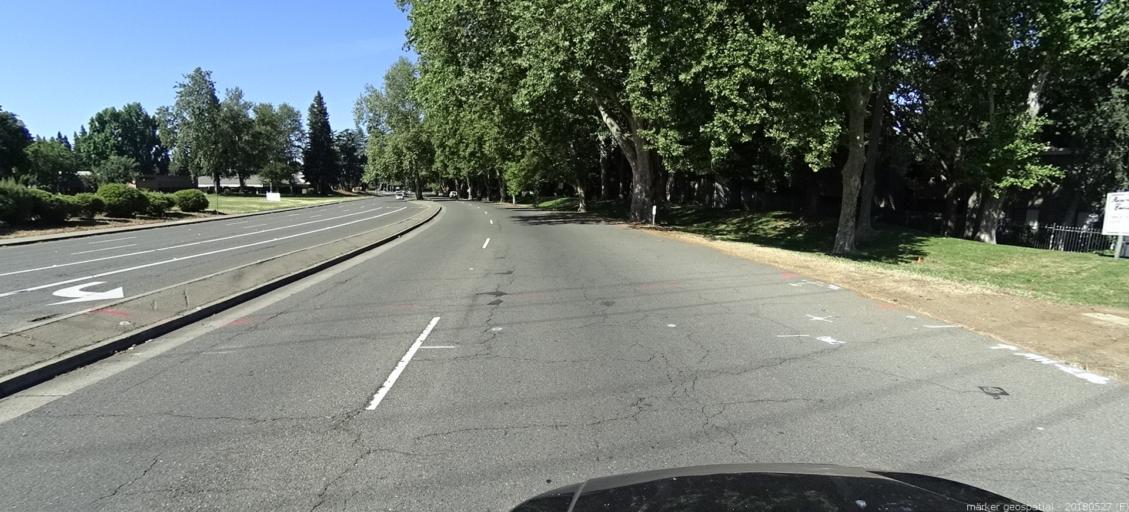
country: US
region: California
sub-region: Sacramento County
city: Arden-Arcade
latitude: 38.5736
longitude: -121.4165
